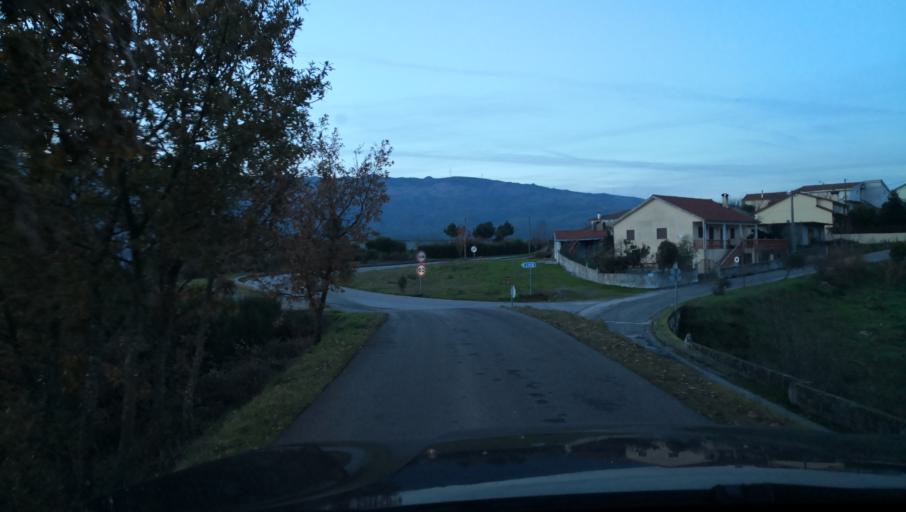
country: PT
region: Vila Real
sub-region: Vila Real
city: Vila Real
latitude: 41.3506
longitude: -7.6993
